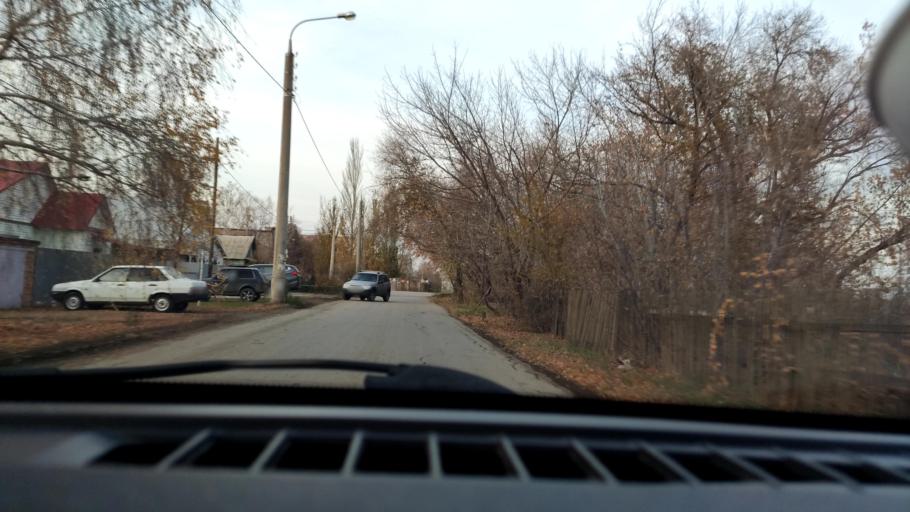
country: RU
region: Samara
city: Samara
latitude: 53.1338
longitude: 50.1357
